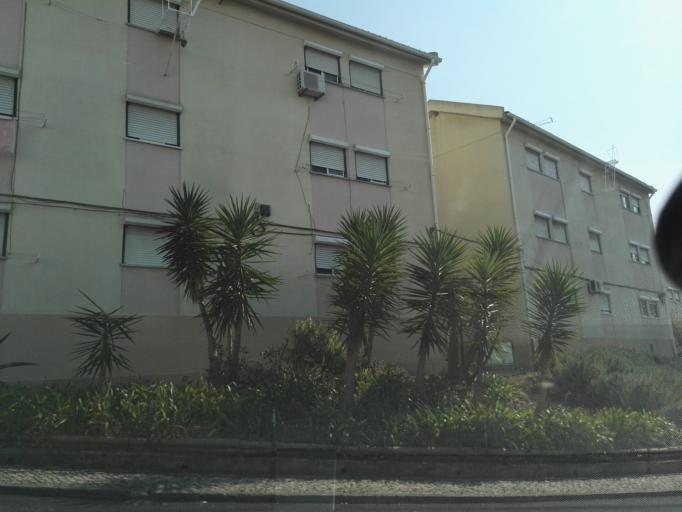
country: PT
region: Lisbon
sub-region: Lisbon
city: Lisbon
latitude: 38.7358
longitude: -9.1150
